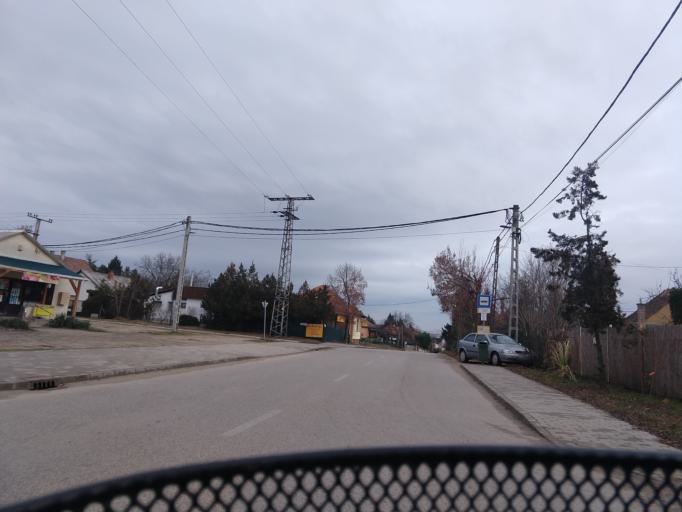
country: HU
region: Pest
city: Veresegyhaz
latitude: 47.6495
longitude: 19.2751
